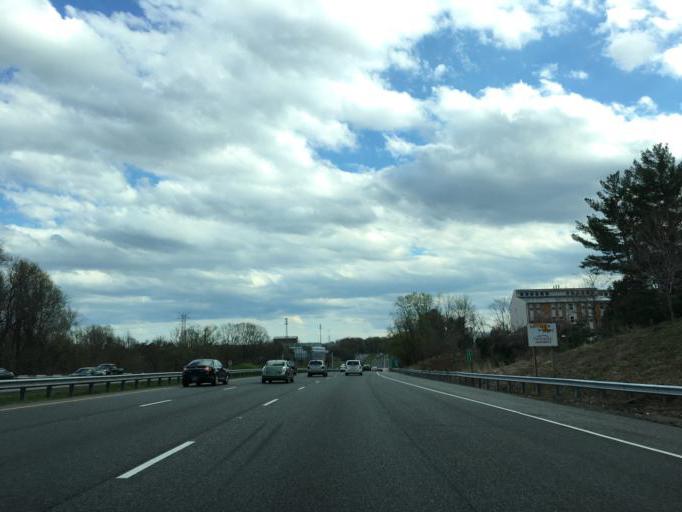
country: US
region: Maryland
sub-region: Baltimore County
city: Mays Chapel
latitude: 39.3894
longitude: -76.6643
